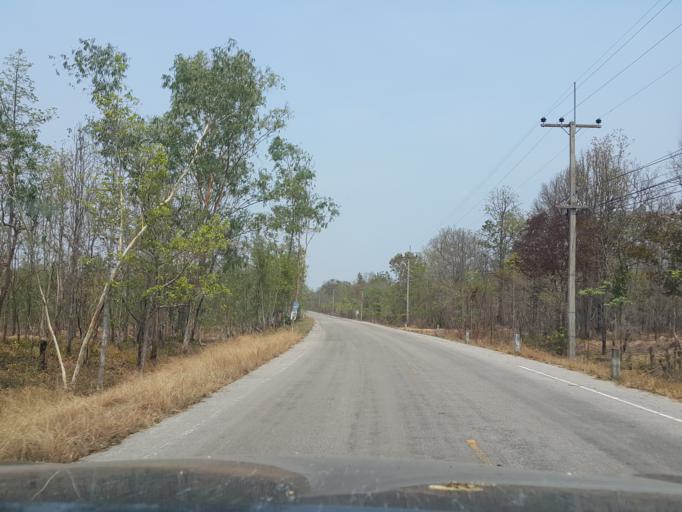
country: TH
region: Lampang
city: Mae Phrik
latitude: 17.5558
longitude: 99.1054
